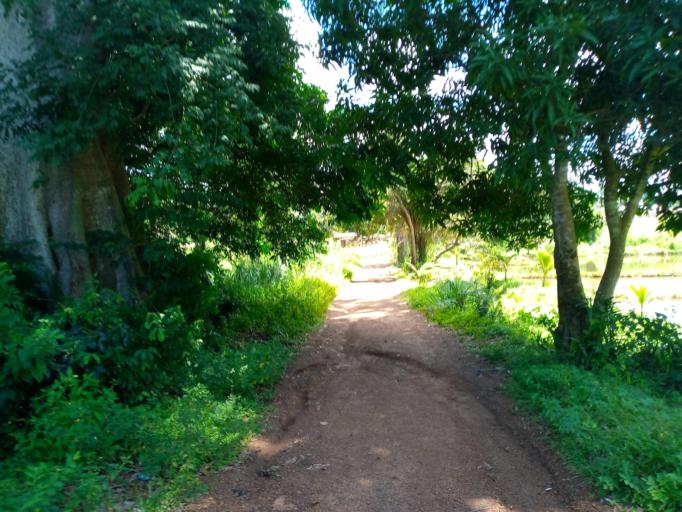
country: SL
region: Northern Province
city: Makeni
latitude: 9.0314
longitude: -12.1608
